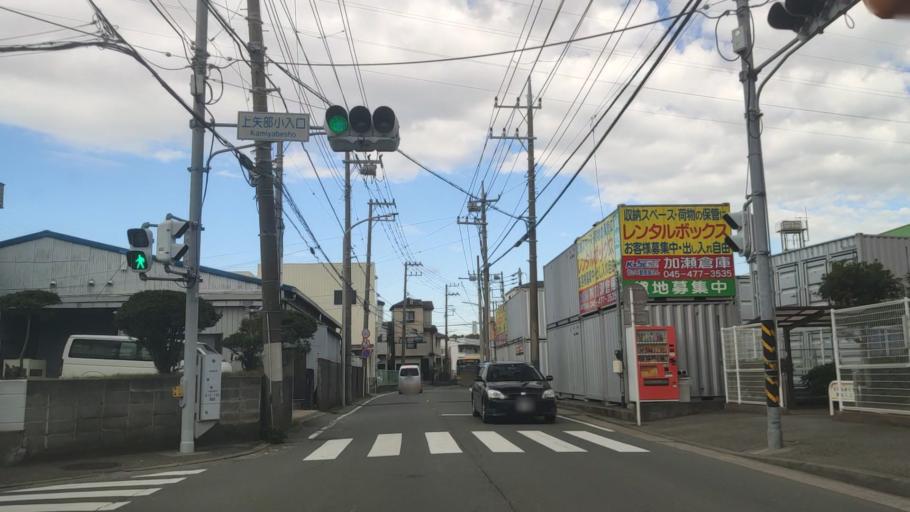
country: JP
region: Kanagawa
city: Minami-rinkan
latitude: 35.4243
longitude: 139.5304
